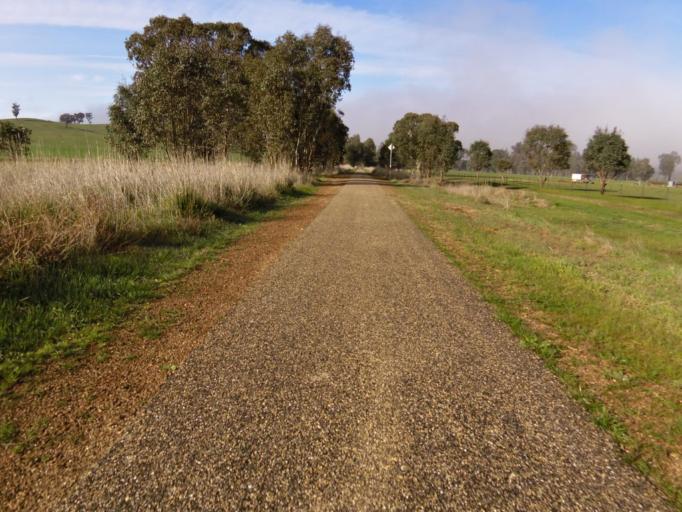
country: AU
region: Victoria
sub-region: Wangaratta
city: Wangaratta
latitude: -36.4410
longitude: 146.5510
